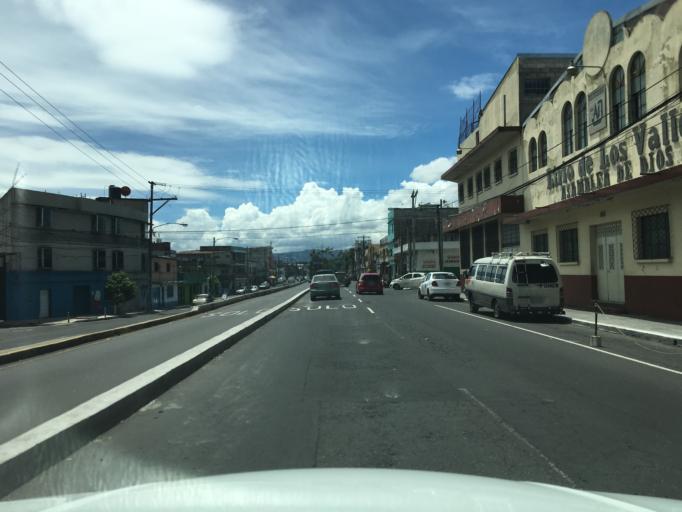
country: GT
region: Guatemala
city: Guatemala City
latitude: 14.6255
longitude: -90.5426
